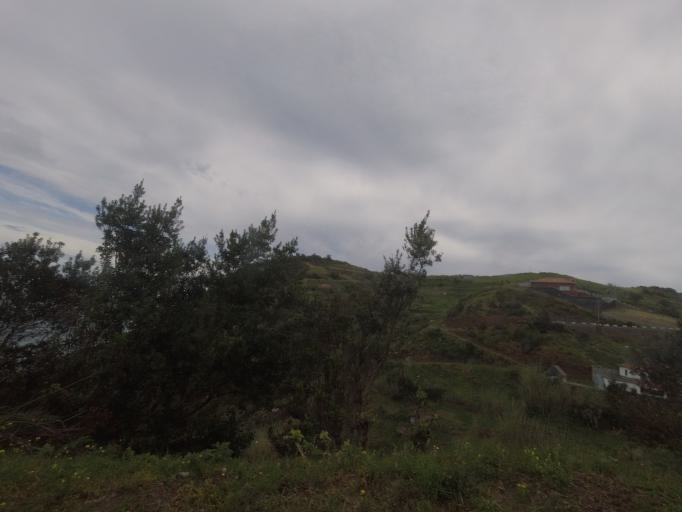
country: PT
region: Madeira
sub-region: Santana
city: Santana
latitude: 32.7654
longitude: -16.8167
